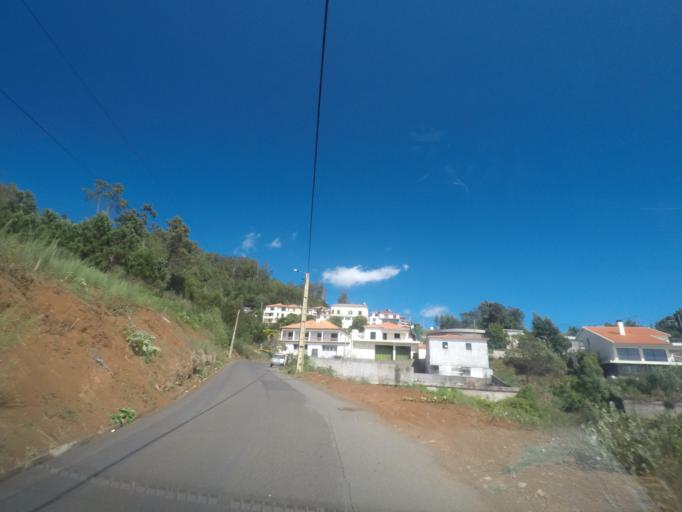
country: PT
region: Madeira
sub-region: Ribeira Brava
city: Campanario
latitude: 32.6799
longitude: -17.0419
